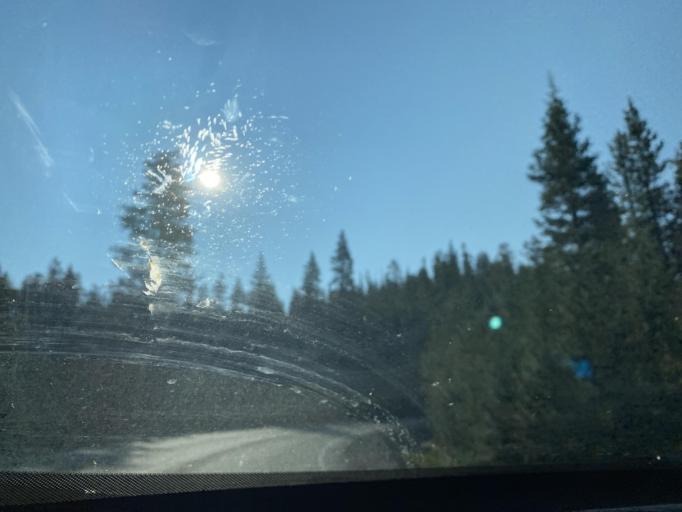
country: US
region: Oregon
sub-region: Deschutes County
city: Three Rivers
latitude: 43.7070
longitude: -121.3179
